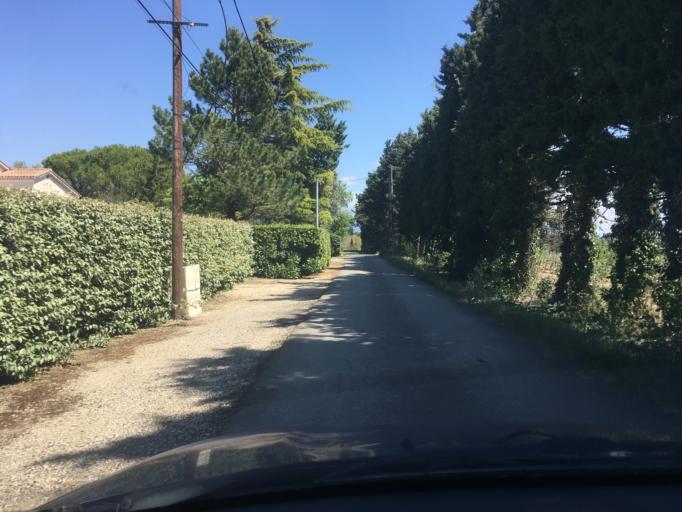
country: FR
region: Provence-Alpes-Cote d'Azur
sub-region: Departement du Vaucluse
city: Jonquieres
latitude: 44.1087
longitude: 4.9295
